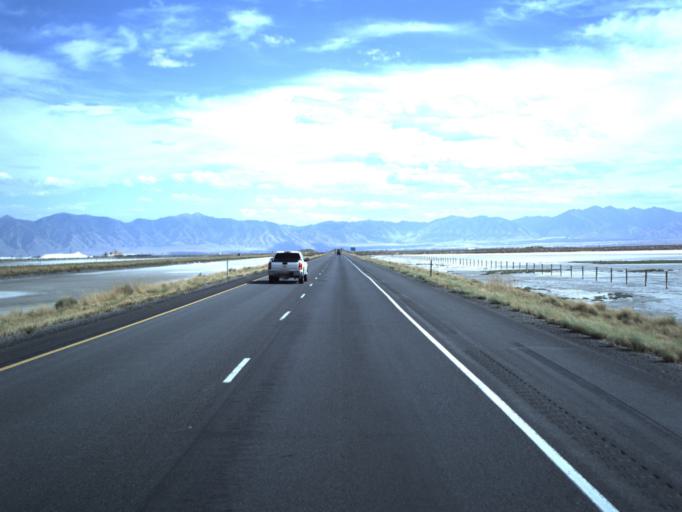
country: US
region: Utah
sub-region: Tooele County
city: Grantsville
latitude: 40.7189
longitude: -112.5524
